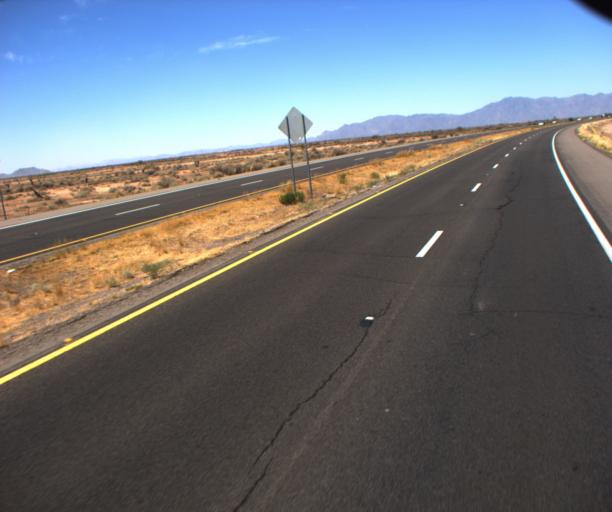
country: US
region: Arizona
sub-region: Maricopa County
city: Sun Lakes
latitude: 33.2529
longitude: -111.9545
